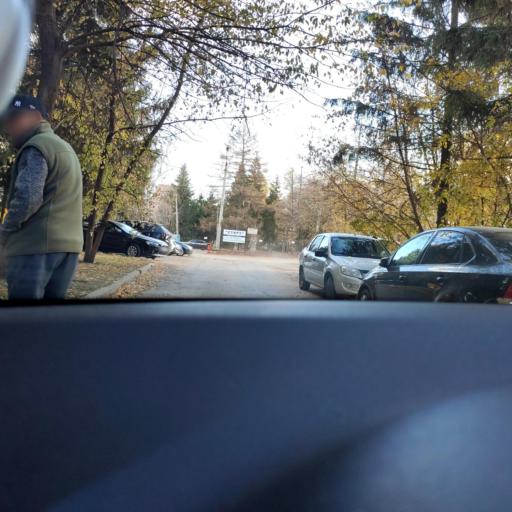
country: RU
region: Samara
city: Samara
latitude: 53.2368
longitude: 50.1835
